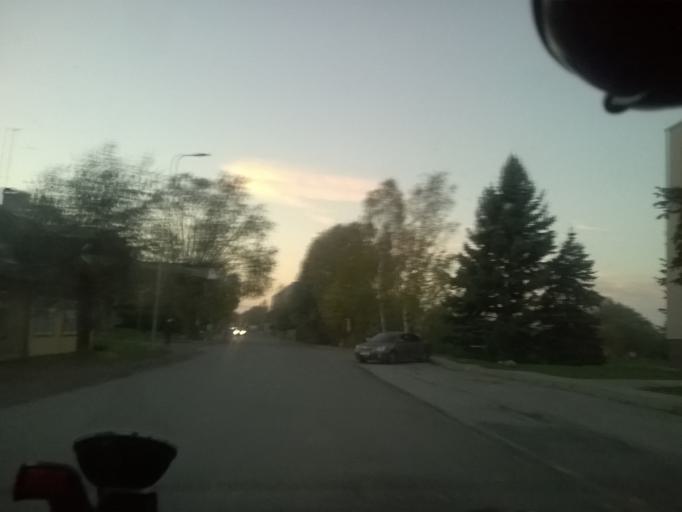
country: EE
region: Laeaene
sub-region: Haapsalu linn
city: Haapsalu
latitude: 58.9411
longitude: 23.5507
